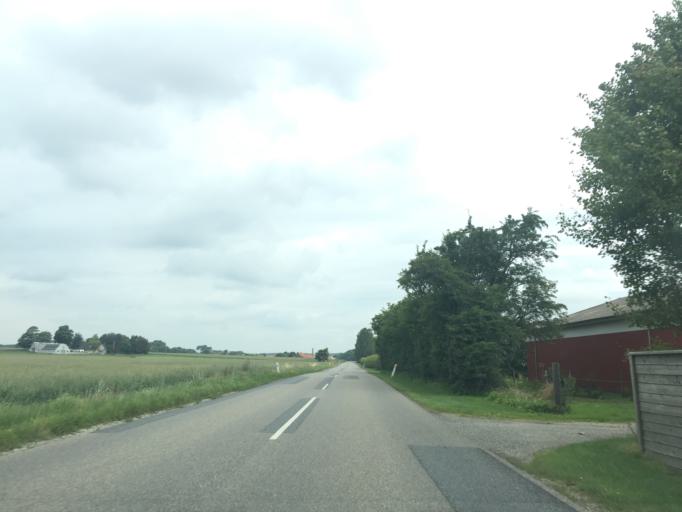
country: DK
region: Central Jutland
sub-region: Favrskov Kommune
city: Ulstrup
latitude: 56.3057
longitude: 9.7651
